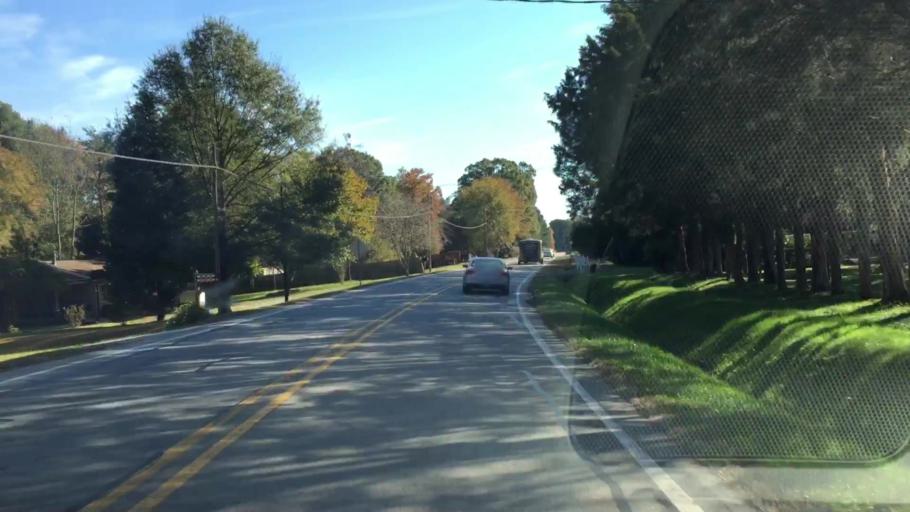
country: US
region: North Carolina
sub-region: Rowan County
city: Salisbury
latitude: 35.6615
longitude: -80.5556
